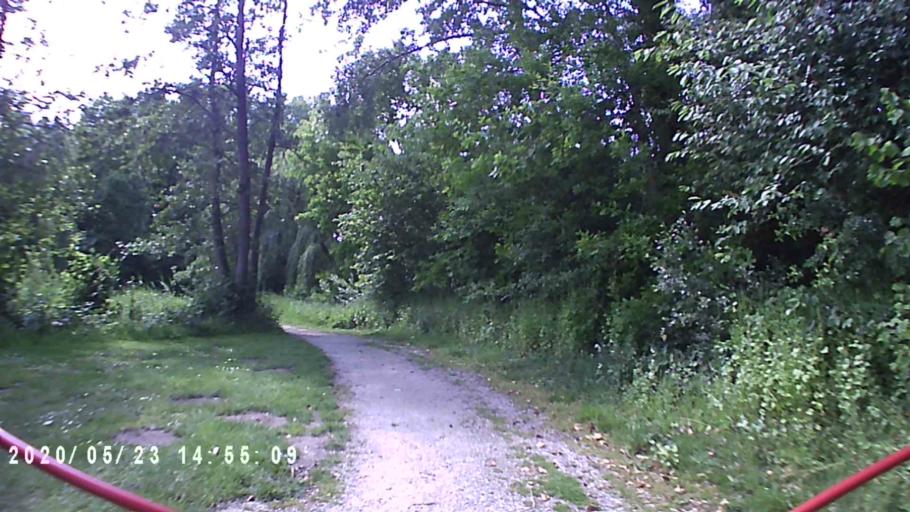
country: NL
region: Groningen
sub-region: Gemeente Delfzijl
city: Delfzijl
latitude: 53.2581
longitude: 6.9240
